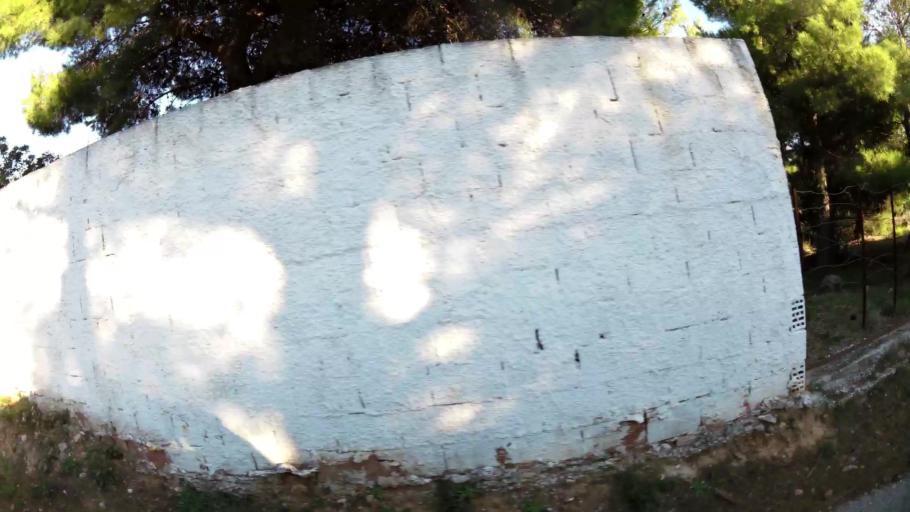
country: GR
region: Attica
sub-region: Nomarchia Athinas
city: Penteli
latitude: 38.0458
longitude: 23.8531
